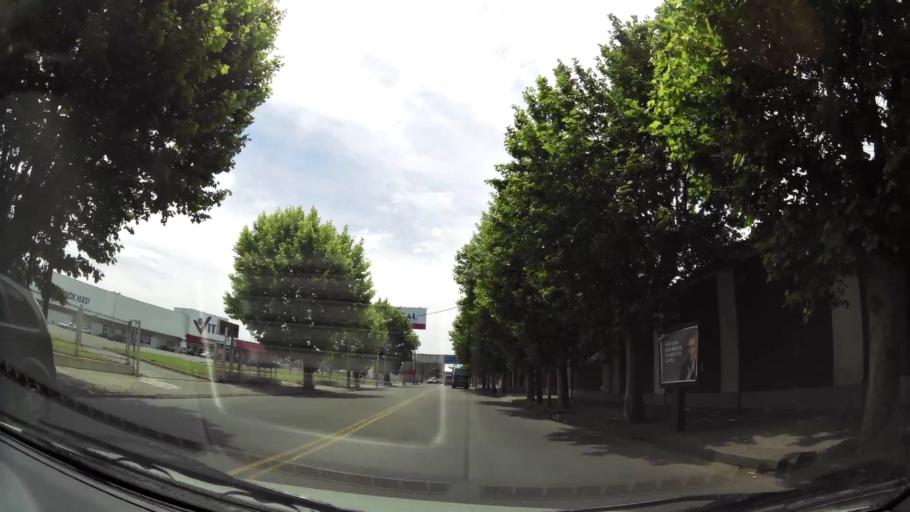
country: AR
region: Buenos Aires
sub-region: Partido de Avellaneda
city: Avellaneda
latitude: -34.6651
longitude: -58.3892
